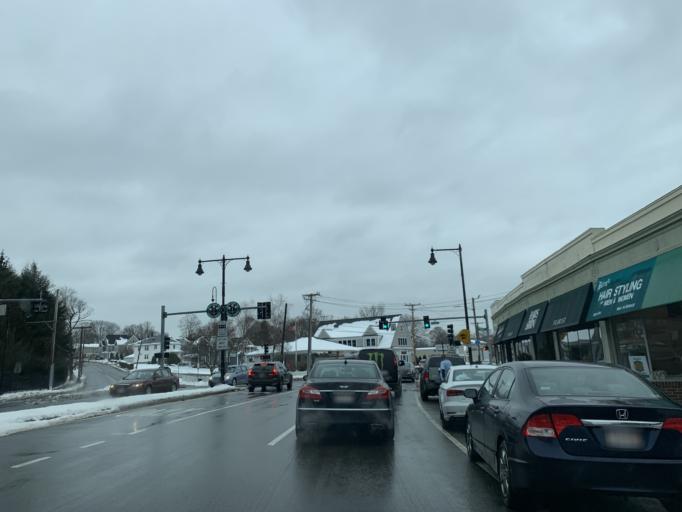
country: US
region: Massachusetts
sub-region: Norfolk County
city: Dedham
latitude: 42.2789
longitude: -71.1594
